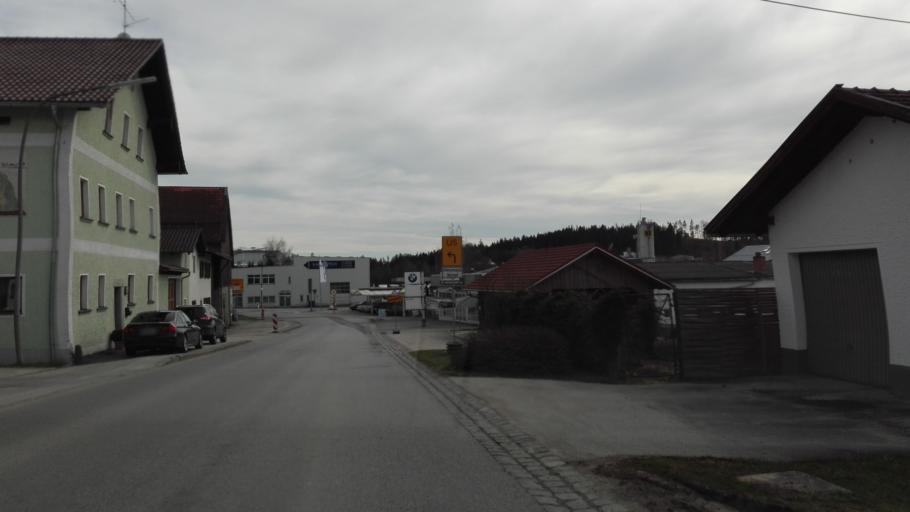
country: DE
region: Bavaria
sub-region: Lower Bavaria
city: Hauzenberg
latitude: 48.6311
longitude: 13.6421
